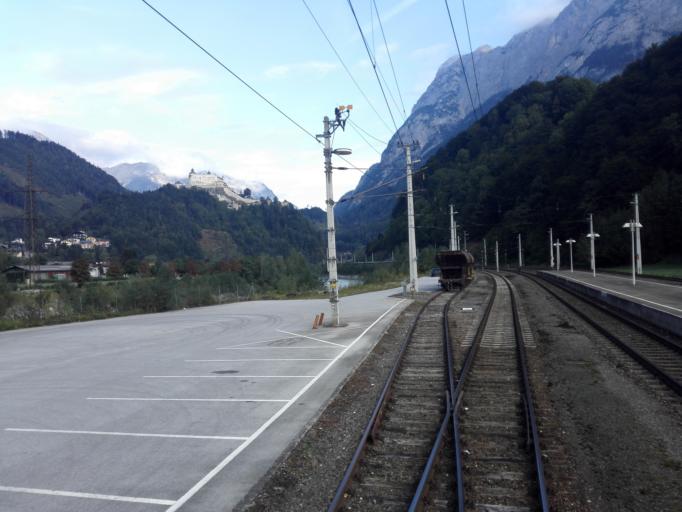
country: AT
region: Salzburg
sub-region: Politischer Bezirk Sankt Johann im Pongau
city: Werfen
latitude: 47.4740
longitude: 13.1952
